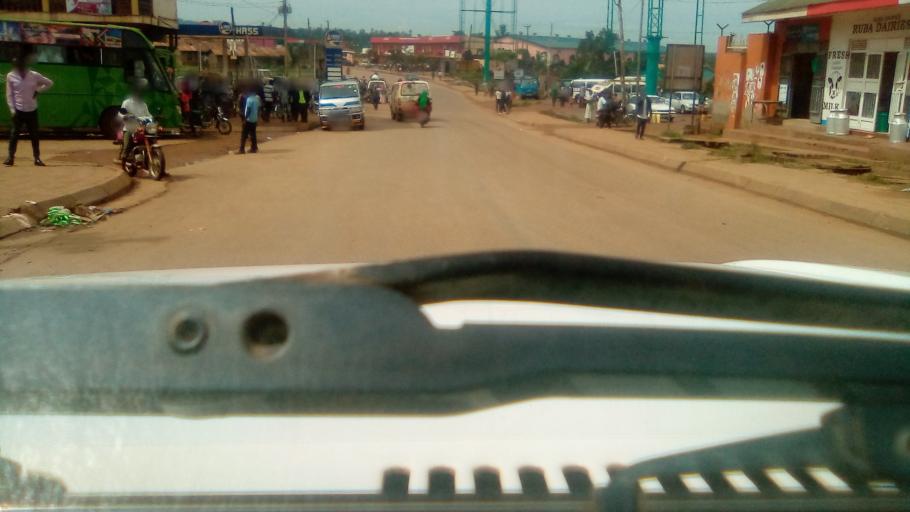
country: UG
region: Eastern Region
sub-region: Mbale District
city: Mbale
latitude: 1.0704
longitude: 34.1753
